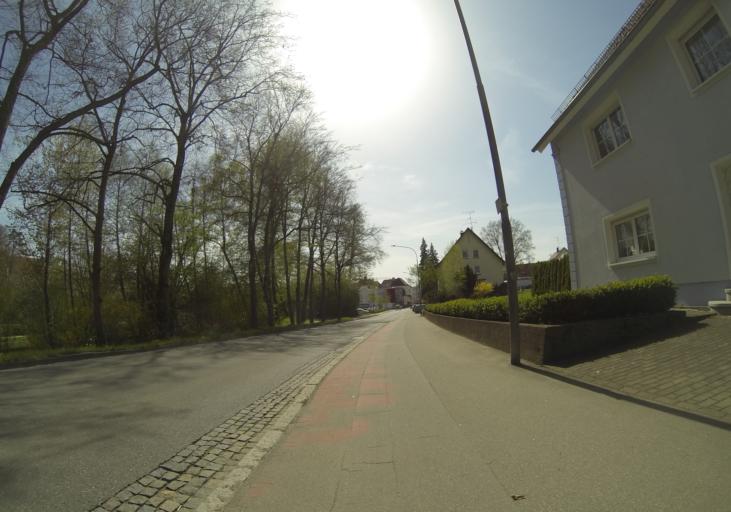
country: DE
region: Baden-Wuerttemberg
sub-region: Tuebingen Region
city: Laupheim
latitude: 48.2320
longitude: 9.8862
